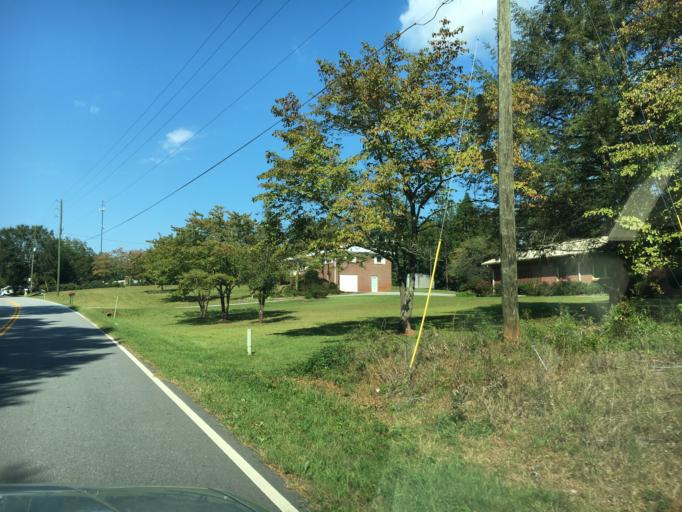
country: US
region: South Carolina
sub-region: Oconee County
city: Utica
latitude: 34.7041
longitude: -82.9269
